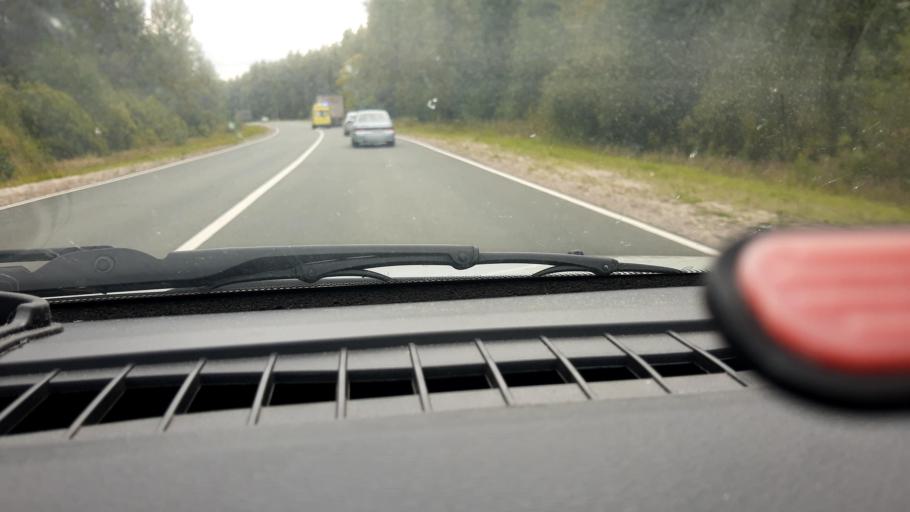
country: RU
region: Nizjnij Novgorod
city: Uren'
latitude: 57.3880
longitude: 45.6863
